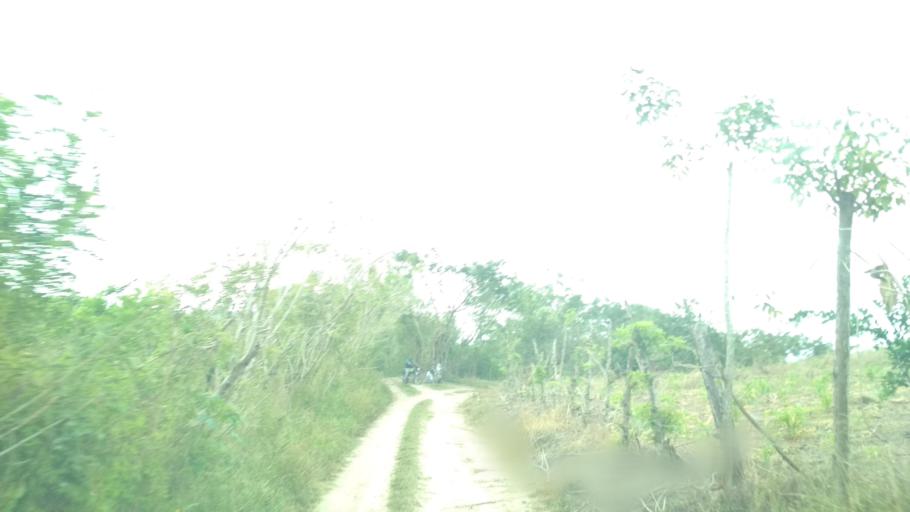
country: MM
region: Kayah
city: Loikaw
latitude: 20.2149
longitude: 97.3315
